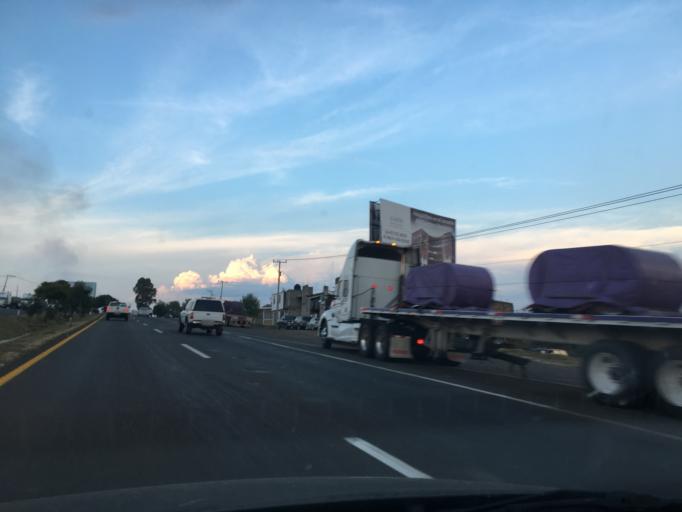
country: MX
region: Michoacan
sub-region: Morelia
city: La Mintzita (Piedra Dura)
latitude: 19.6243
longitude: -101.2790
